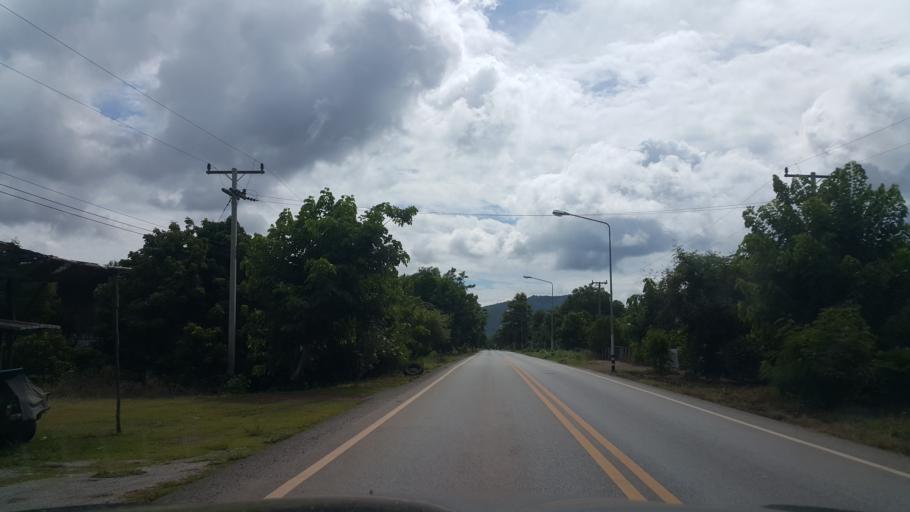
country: TH
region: Uttaradit
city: Thong Saen Khan
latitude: 17.3961
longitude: 100.3007
